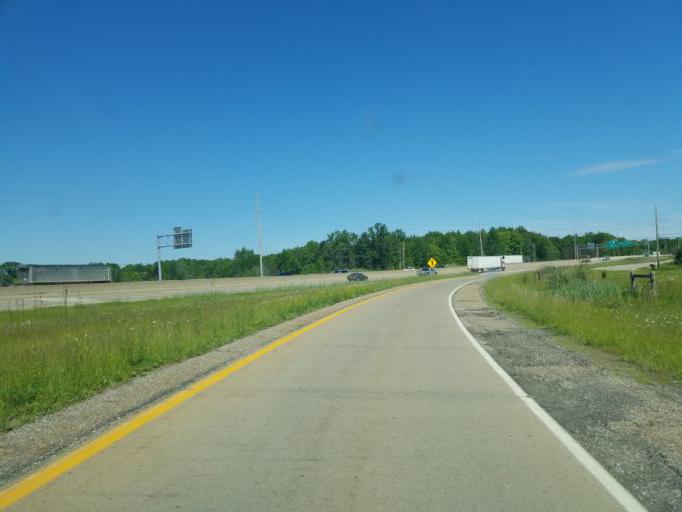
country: US
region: Ohio
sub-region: Summit County
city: Boston Heights
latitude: 41.2372
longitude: -81.4932
